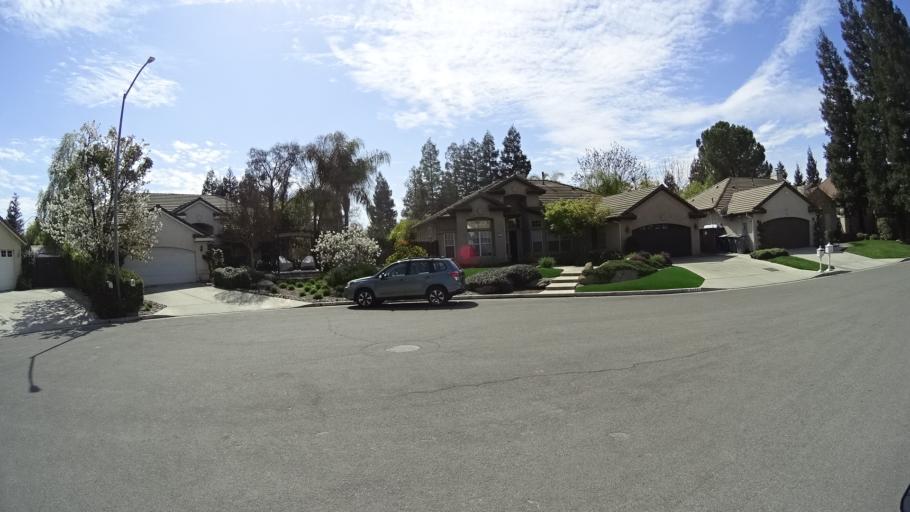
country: US
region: California
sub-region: Fresno County
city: Biola
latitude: 36.8480
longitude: -119.8887
